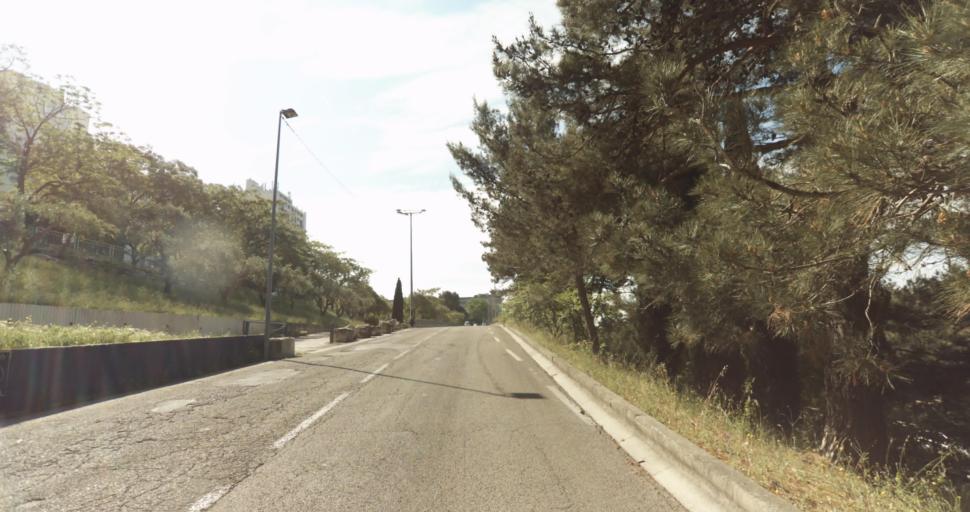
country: FR
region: Languedoc-Roussillon
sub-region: Departement du Gard
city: Nimes
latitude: 43.8295
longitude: 4.3259
